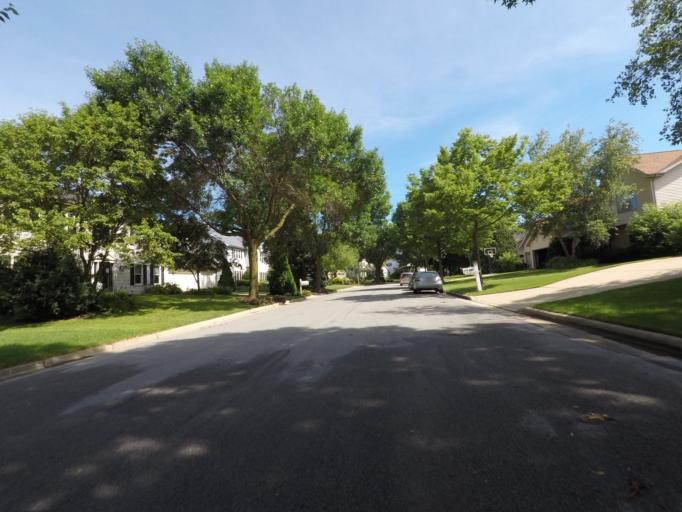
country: US
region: Wisconsin
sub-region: Dane County
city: Middleton
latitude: 43.0821
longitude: -89.5175
